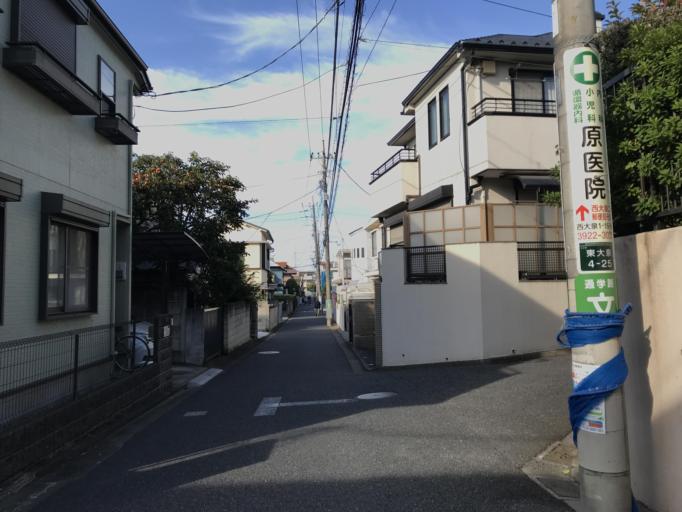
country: JP
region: Tokyo
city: Musashino
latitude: 35.7522
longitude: 139.5831
